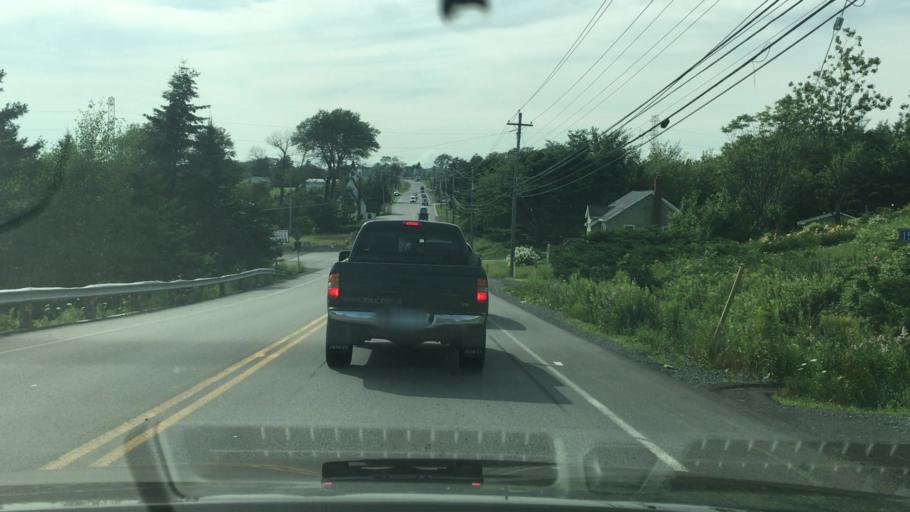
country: CA
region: Nova Scotia
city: Dartmouth
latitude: 44.7313
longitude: -63.7558
